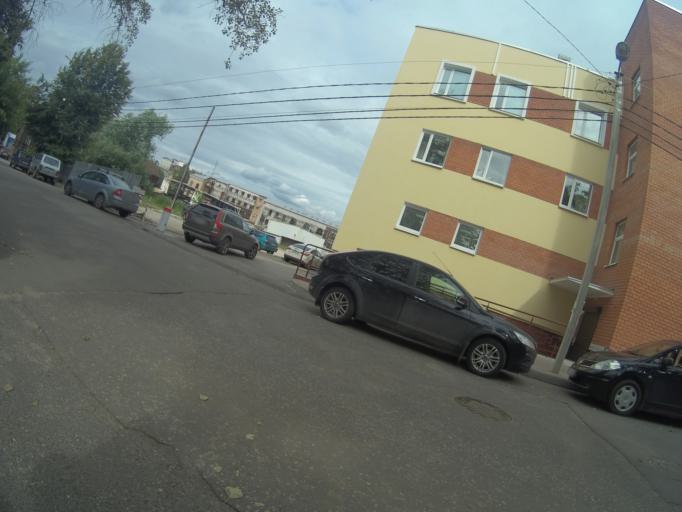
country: RU
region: Vladimir
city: Vladimir
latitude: 56.1286
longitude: 40.3906
